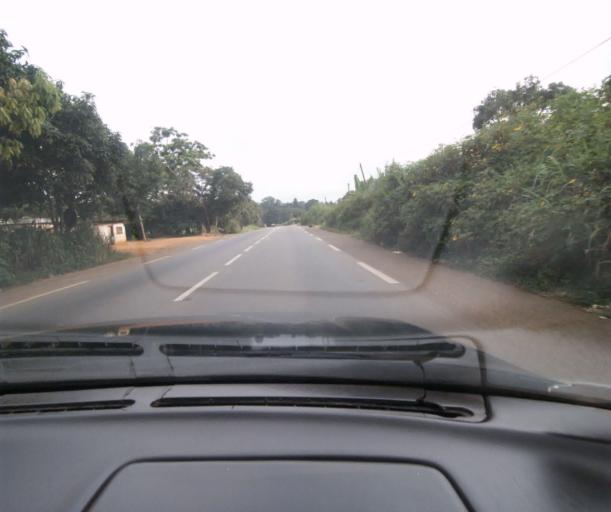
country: CM
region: Centre
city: Obala
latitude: 4.0827
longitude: 11.5489
